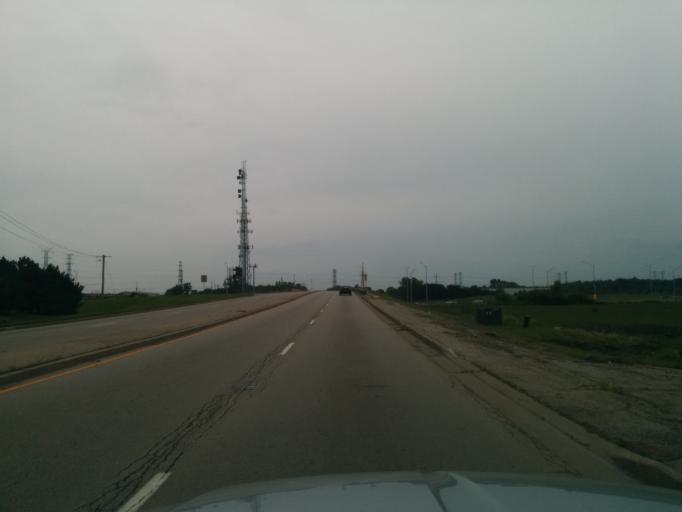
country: US
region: Illinois
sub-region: DuPage County
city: Warrenville
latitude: 41.8031
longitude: -88.2398
